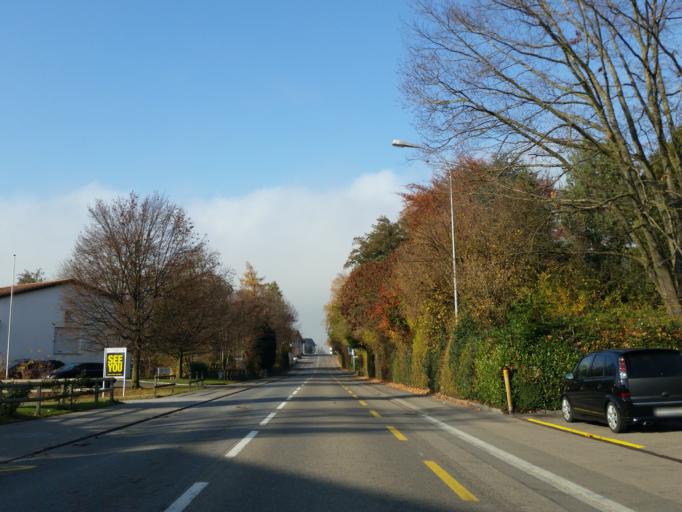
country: CH
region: Thurgau
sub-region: Arbon District
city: Arbon
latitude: 47.5252
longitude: 9.4087
